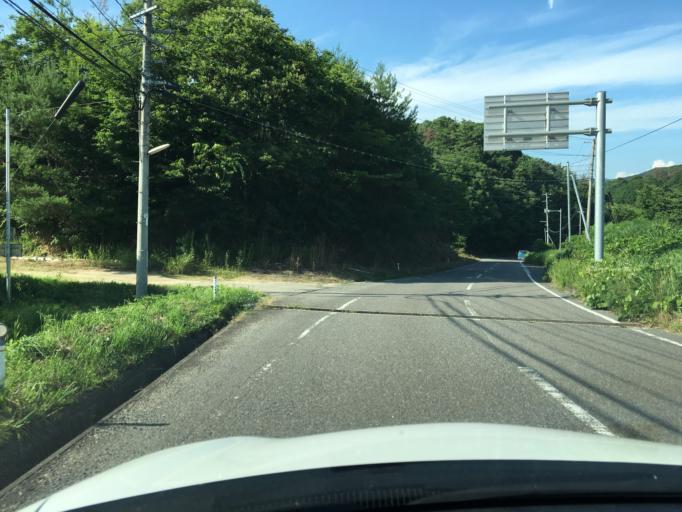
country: JP
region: Fukushima
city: Ishikawa
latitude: 37.2053
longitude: 140.4805
